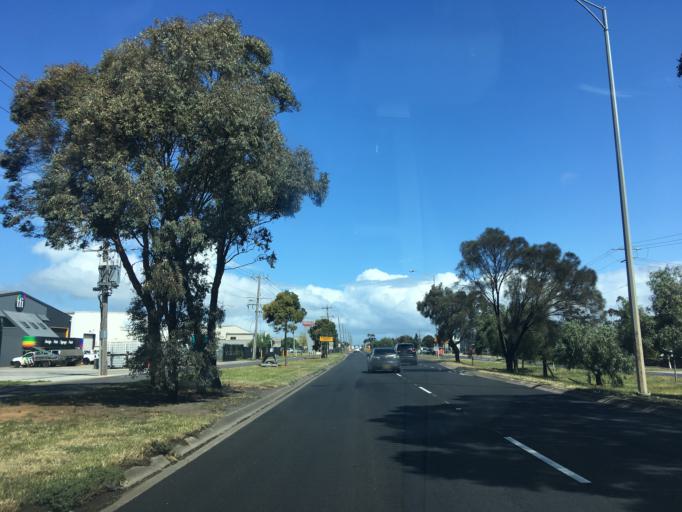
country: AU
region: Victoria
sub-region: Brimbank
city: Derrimut
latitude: -37.8219
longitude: 144.7864
